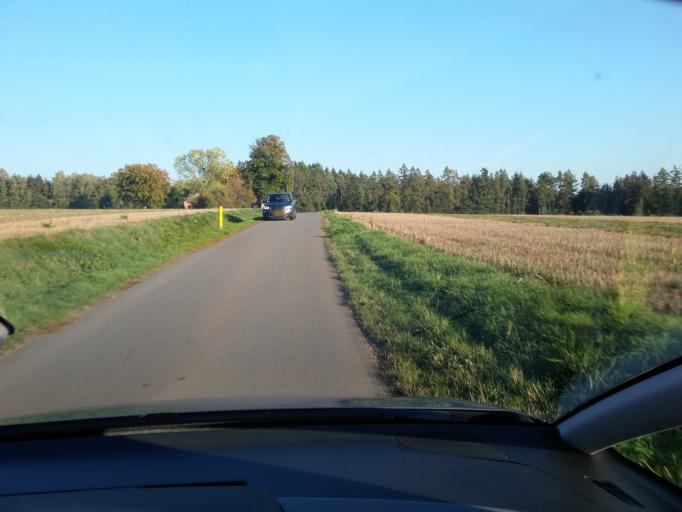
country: LU
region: Luxembourg
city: Eischen
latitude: 49.6845
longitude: 5.8578
